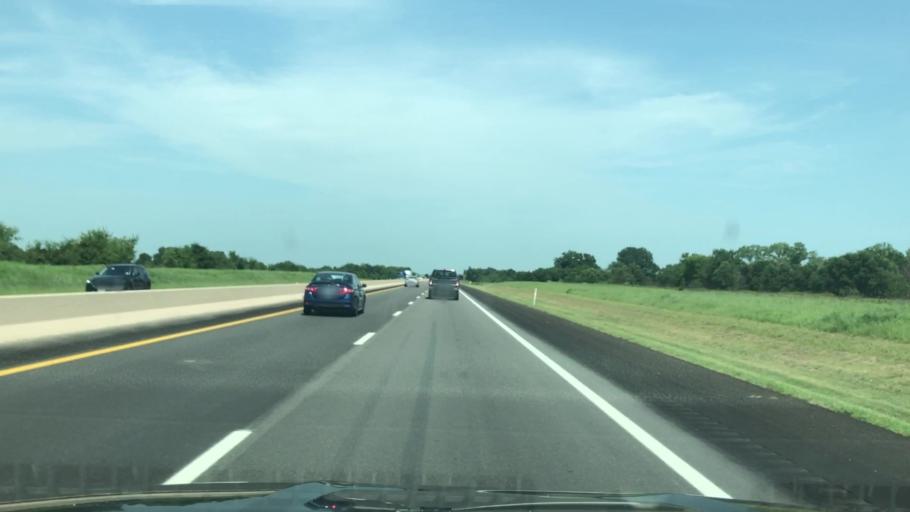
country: US
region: Oklahoma
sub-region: Craig County
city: Vinita
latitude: 36.6651
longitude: -95.0802
